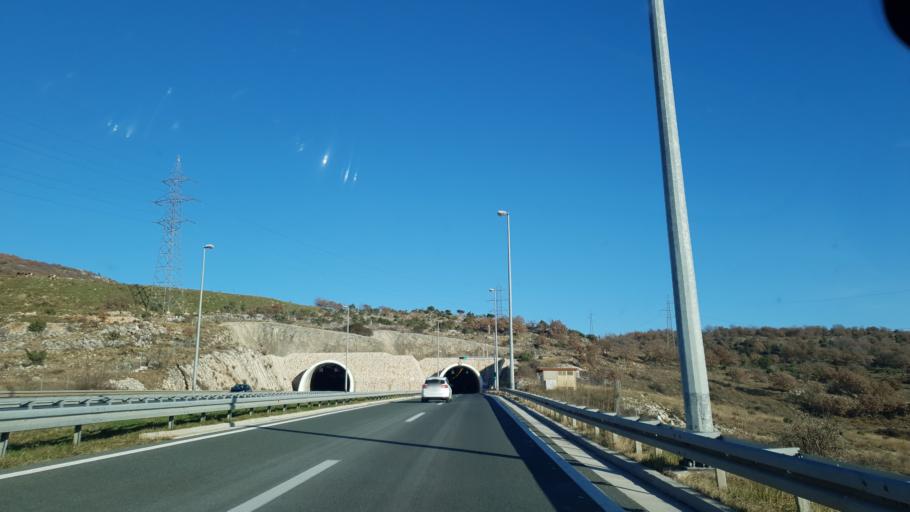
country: HR
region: Splitsko-Dalmatinska
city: Dugopolje
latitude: 43.6043
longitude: 16.5837
